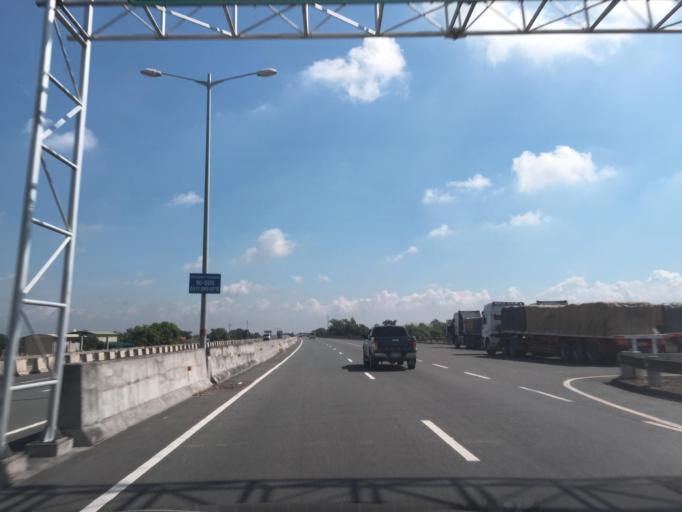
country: PH
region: Central Luzon
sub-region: Province of Tarlac
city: Concepcion
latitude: 15.3362
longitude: 120.6753
